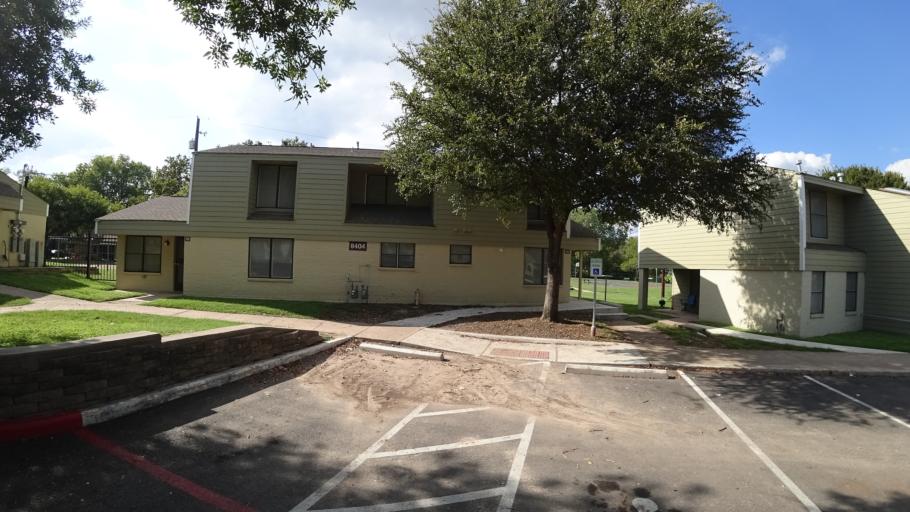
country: US
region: Texas
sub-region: Travis County
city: Austin
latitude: 30.3540
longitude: -97.7084
